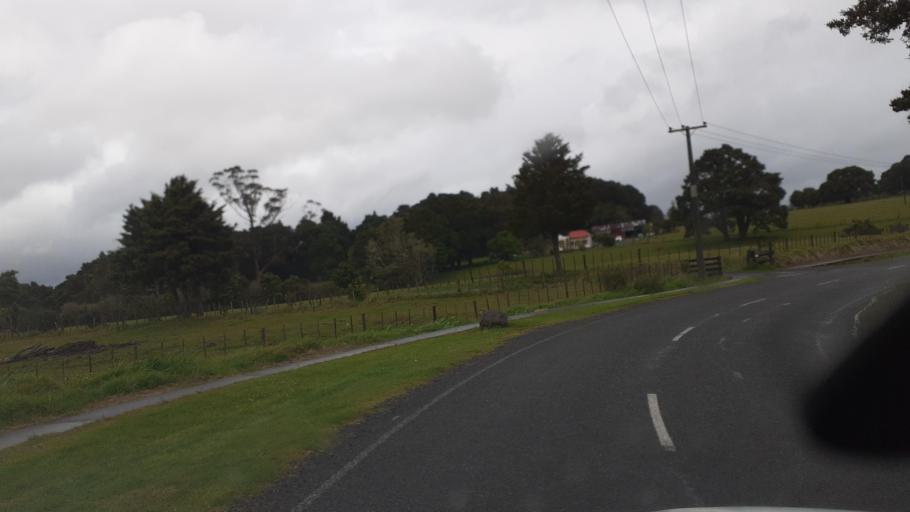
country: NZ
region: Northland
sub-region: Far North District
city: Waimate North
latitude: -35.4171
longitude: 173.8001
